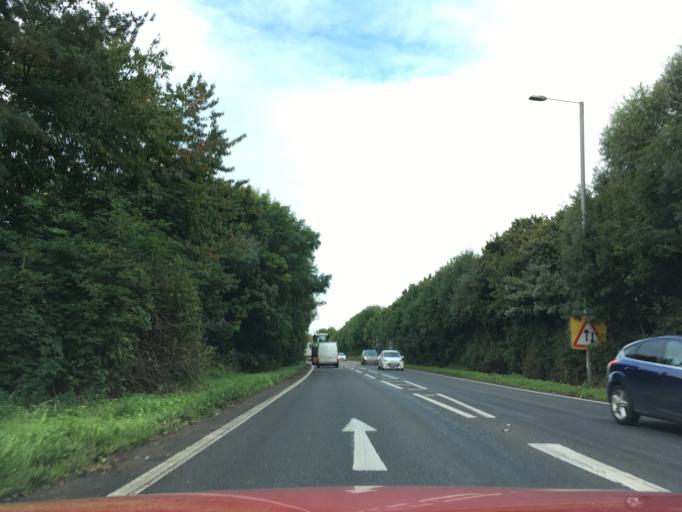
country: GB
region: England
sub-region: Gloucestershire
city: Gloucester
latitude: 51.8825
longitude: -2.2395
